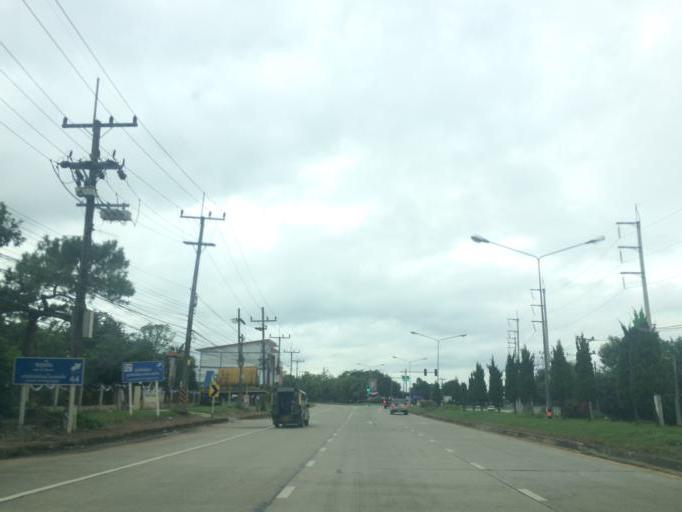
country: TH
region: Chiang Rai
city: Mae Chan
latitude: 20.1367
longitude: 99.8581
